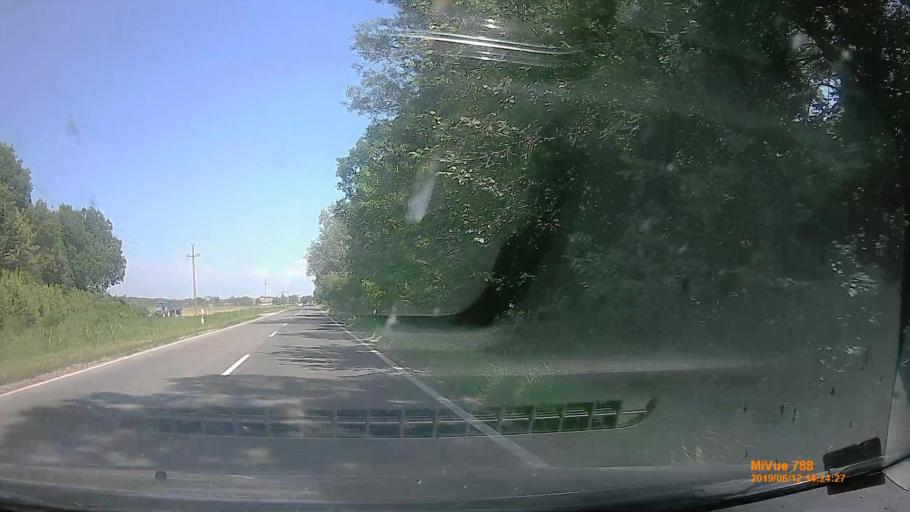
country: HU
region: Csongrad
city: Maroslele
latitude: 46.2184
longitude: 20.3119
